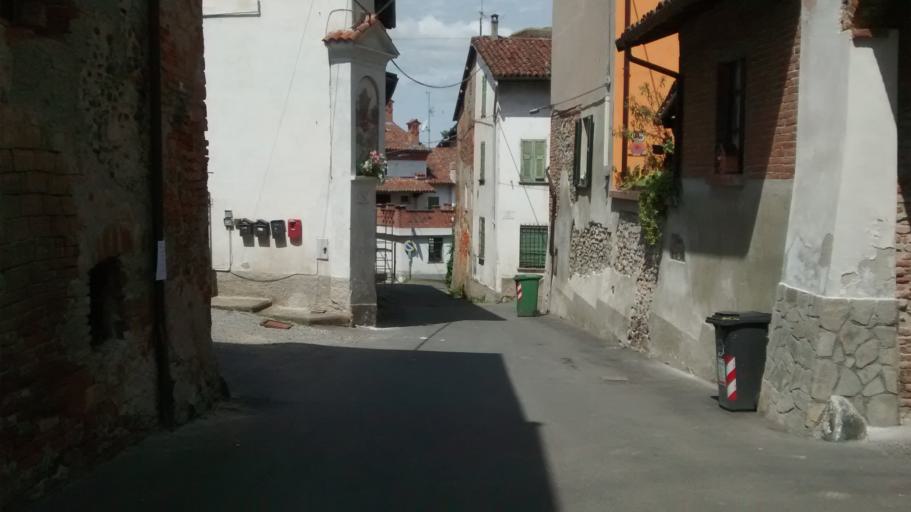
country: IT
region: Piedmont
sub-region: Provincia di Alessandria
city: Capriata d'Orba
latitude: 44.7315
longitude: 8.6889
